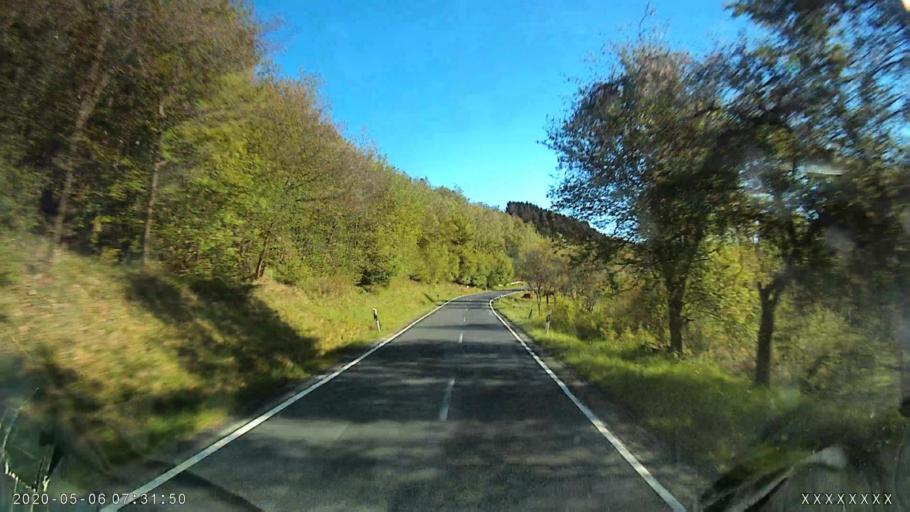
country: DE
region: Hesse
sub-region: Regierungsbezirk Giessen
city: Haiger
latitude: 50.8195
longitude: 8.2210
